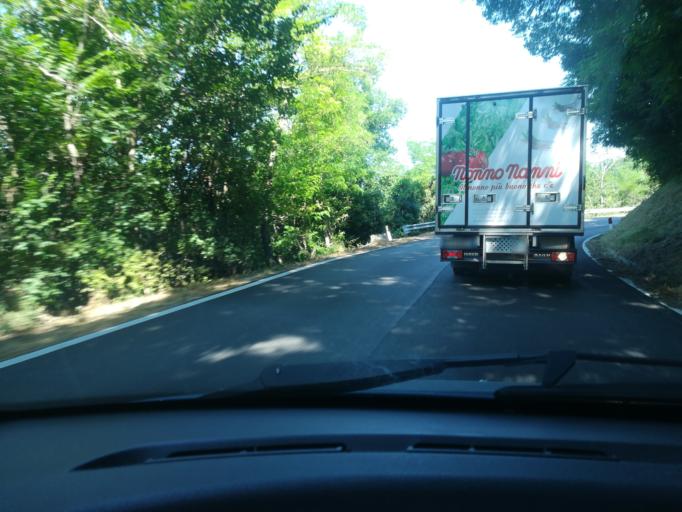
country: IT
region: The Marches
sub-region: Provincia di Macerata
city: San Ginesio
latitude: 43.1080
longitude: 13.3511
